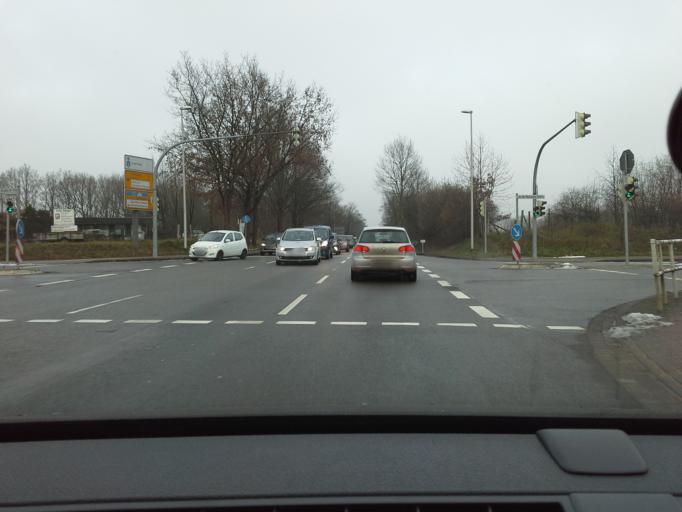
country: DE
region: Schleswig-Holstein
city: Quickborn
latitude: 53.7354
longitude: 9.9035
